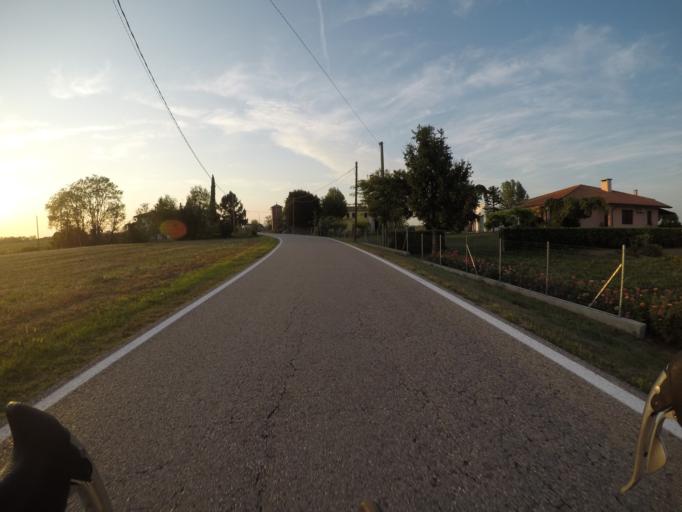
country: IT
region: Veneto
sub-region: Provincia di Rovigo
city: San Bellino
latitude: 45.0061
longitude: 11.5740
